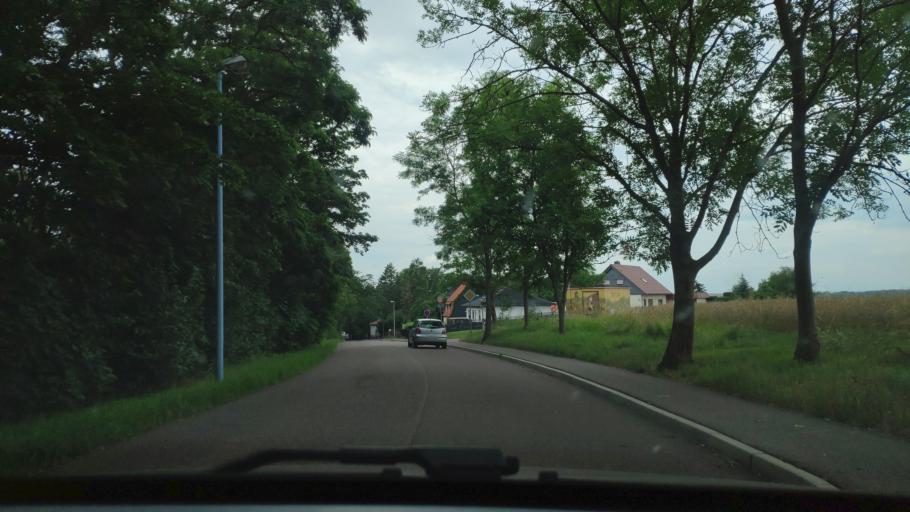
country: DE
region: Saxony-Anhalt
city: Bernburg
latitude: 51.7920
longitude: 11.7127
